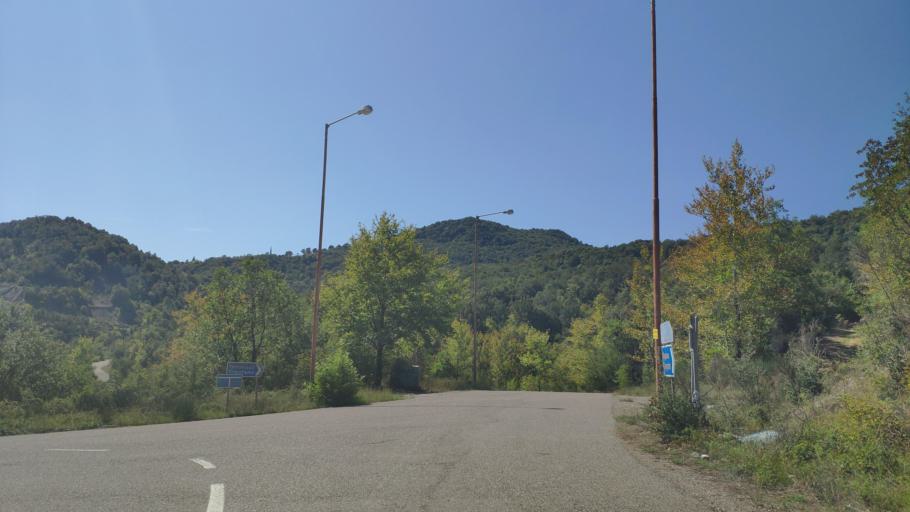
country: GR
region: Central Greece
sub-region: Nomos Evrytanias
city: Kerasochori
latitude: 38.9952
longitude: 21.5550
